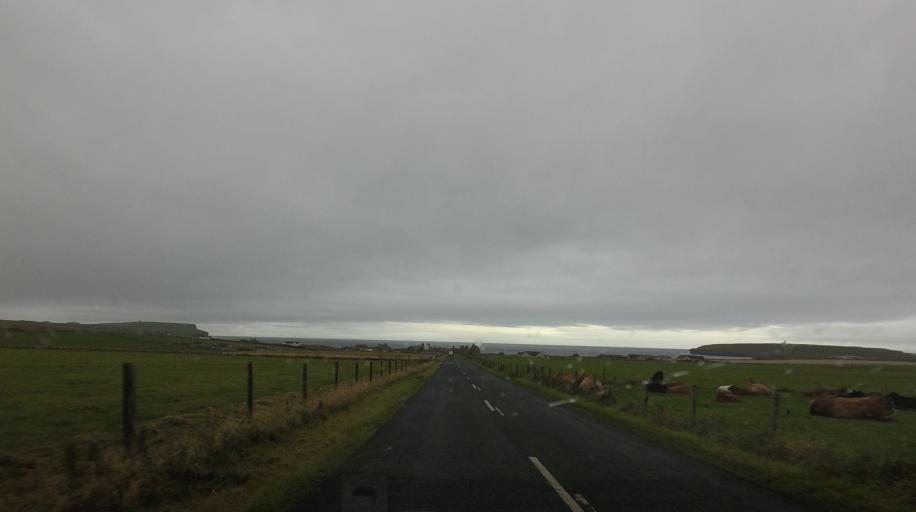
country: GB
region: Scotland
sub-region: Orkney Islands
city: Stromness
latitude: 59.1310
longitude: -3.3058
